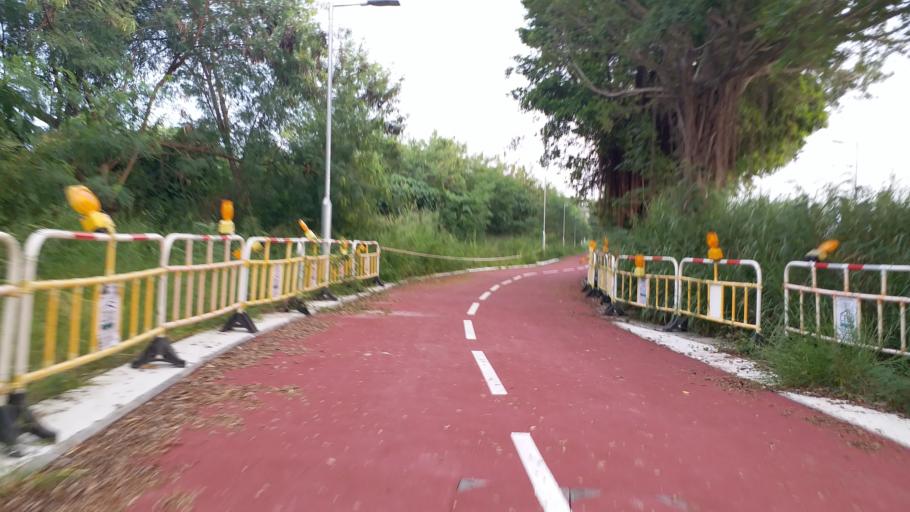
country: HK
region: Yuen Long
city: Yuen Long Kau Hui
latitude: 22.4636
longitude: 114.0451
